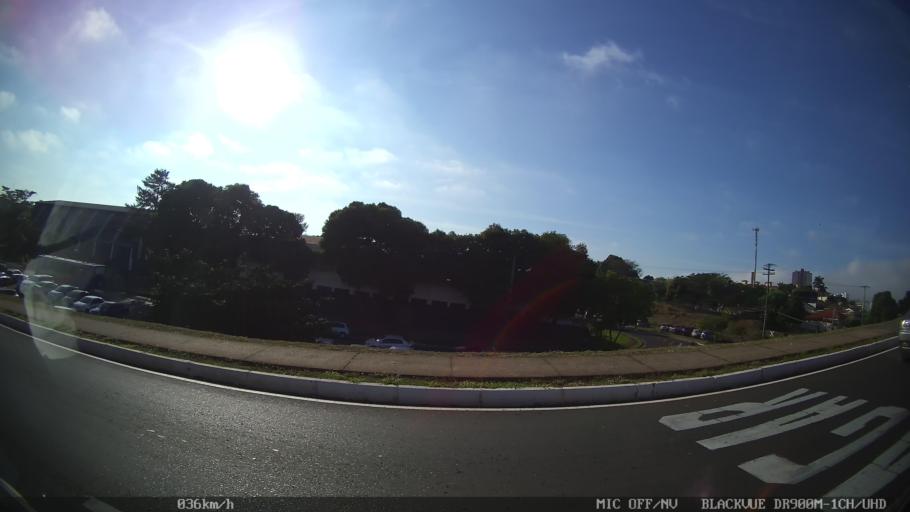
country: BR
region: Sao Paulo
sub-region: Sao Jose Do Rio Preto
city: Sao Jose do Rio Preto
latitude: -20.8111
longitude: -49.3673
